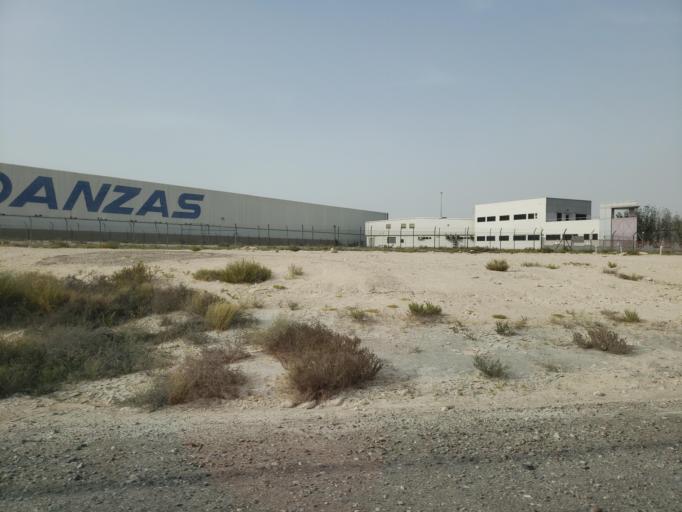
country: AE
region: Dubai
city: Dubai
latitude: 24.9499
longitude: 55.0671
